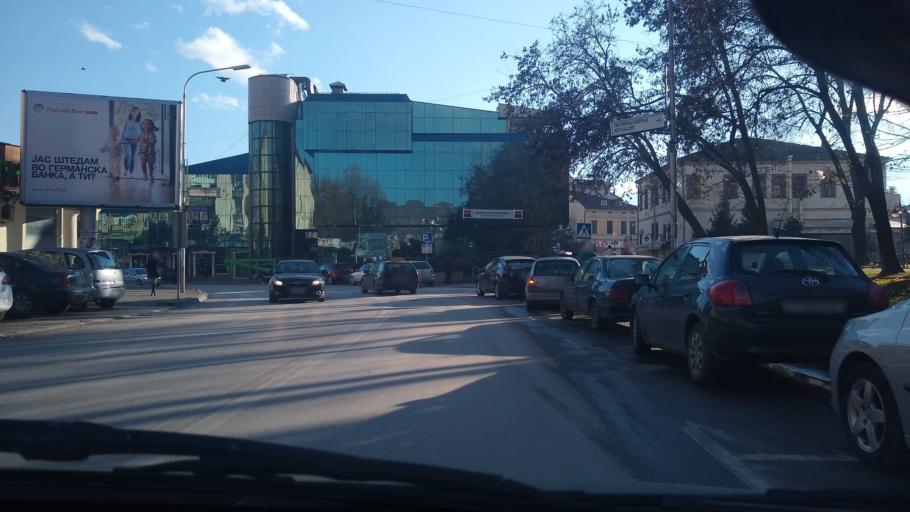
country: MK
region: Bitola
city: Bitola
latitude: 41.0310
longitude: 21.3354
